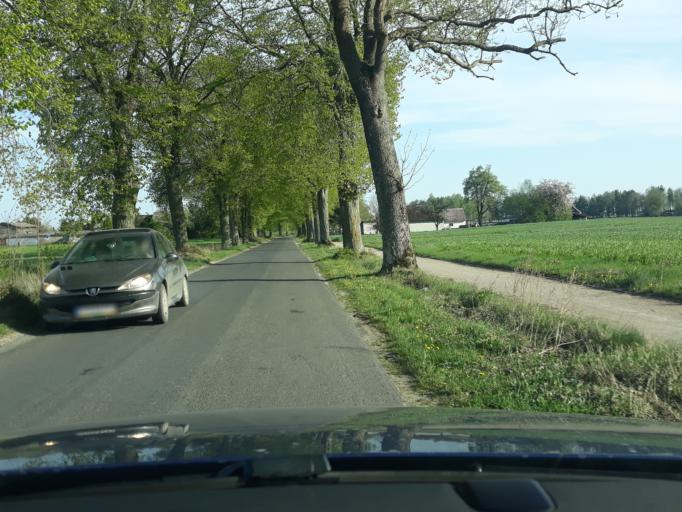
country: PL
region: Pomeranian Voivodeship
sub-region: Powiat czluchowski
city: Przechlewo
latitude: 53.8367
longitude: 17.3657
